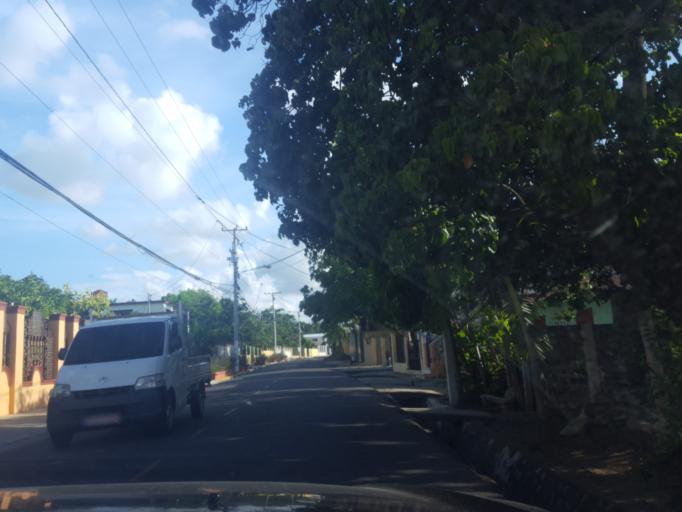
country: DO
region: Santiago
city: Licey al Medio
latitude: 19.3854
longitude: -70.6304
